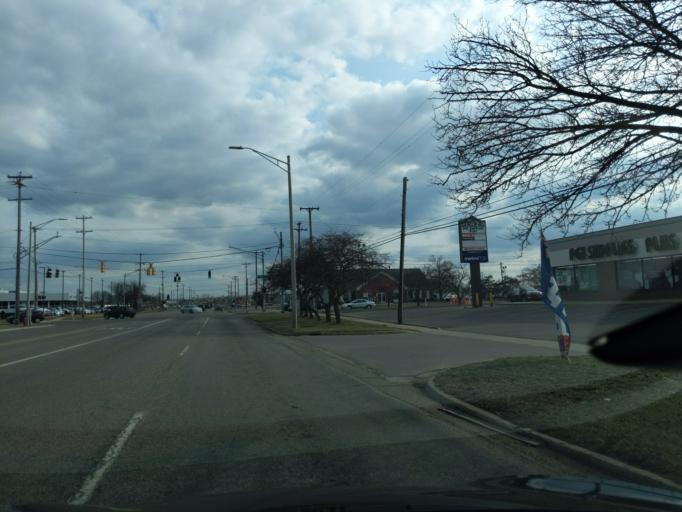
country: US
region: Michigan
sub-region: Ingham County
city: Holt
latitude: 42.6699
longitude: -84.5382
